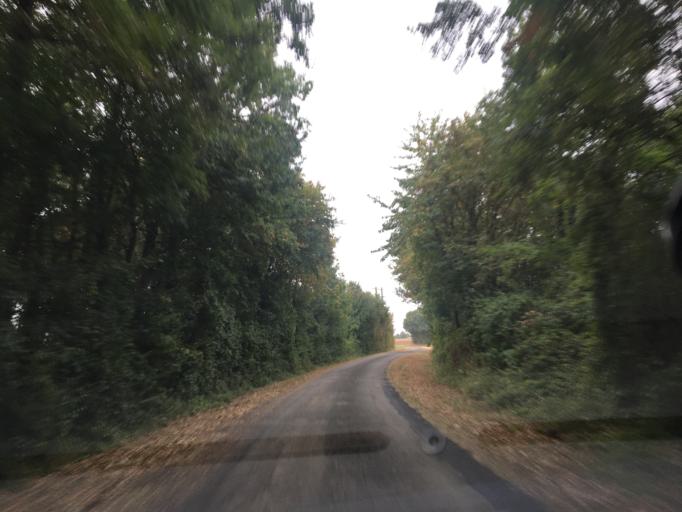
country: FR
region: Poitou-Charentes
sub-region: Departement des Deux-Sevres
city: Beauvoir-sur-Niort
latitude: 46.0810
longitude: -0.5223
